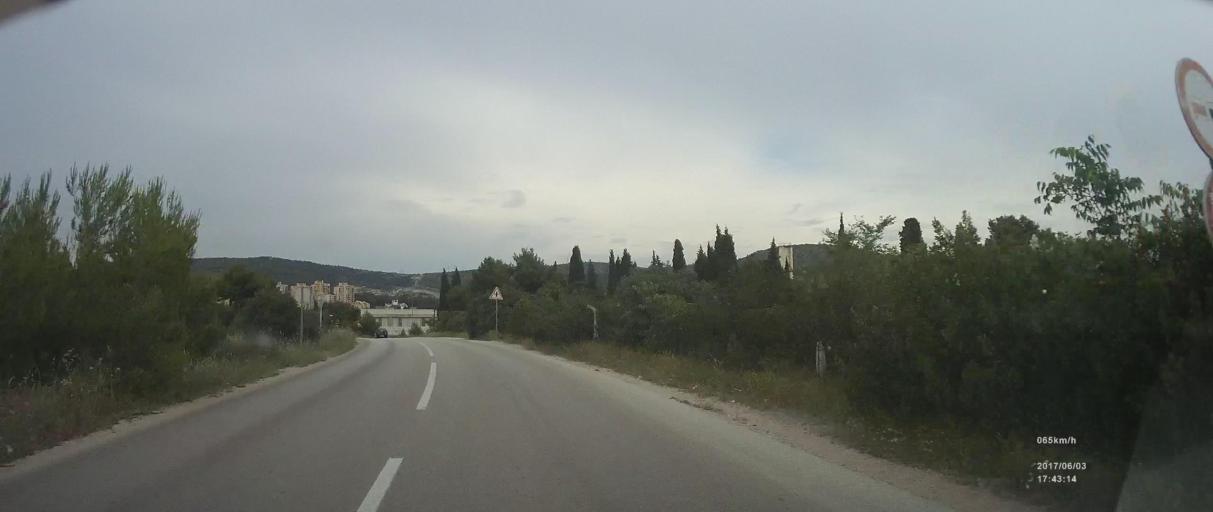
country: HR
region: Sibensko-Kniniska
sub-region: Grad Sibenik
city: Sibenik
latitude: 43.7131
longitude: 15.9050
